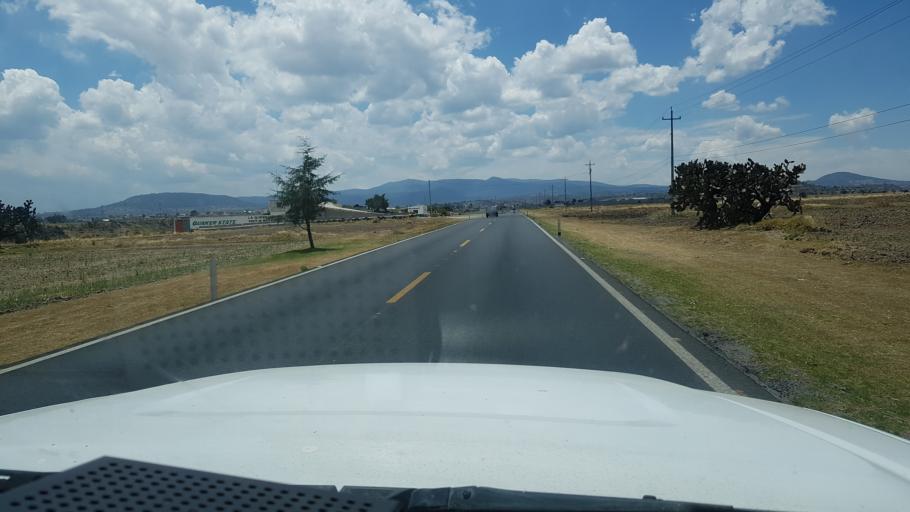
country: MX
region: Hidalgo
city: Calpulalpan
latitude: 19.6097
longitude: -98.5594
